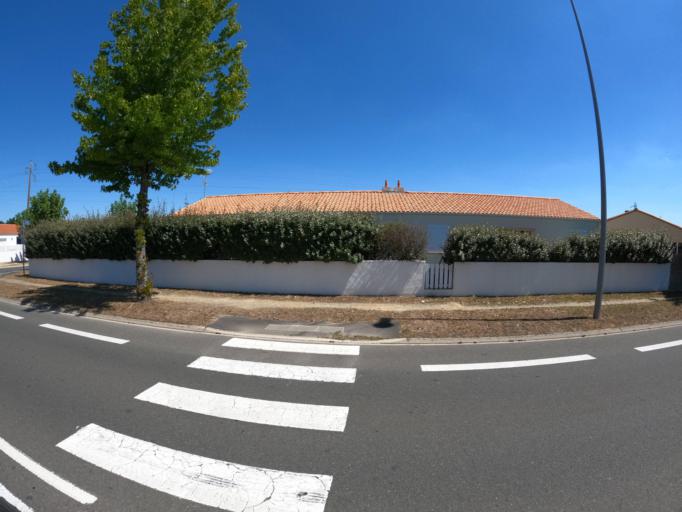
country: FR
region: Pays de la Loire
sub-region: Departement de la Vendee
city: Challans
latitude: 46.8458
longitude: -1.8593
